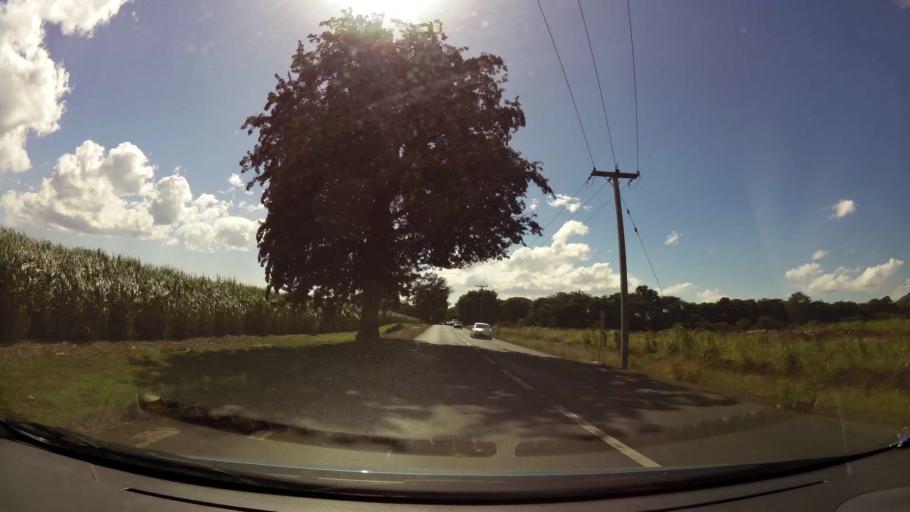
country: MU
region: Black River
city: Cascavelle
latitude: -20.2658
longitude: 57.4068
